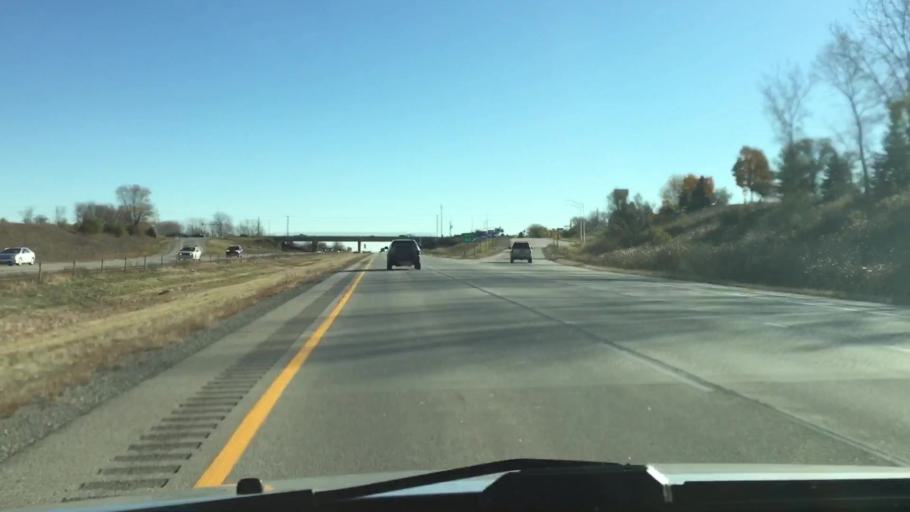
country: US
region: Wisconsin
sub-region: Outagamie County
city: Appleton
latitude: 44.2986
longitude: -88.4207
